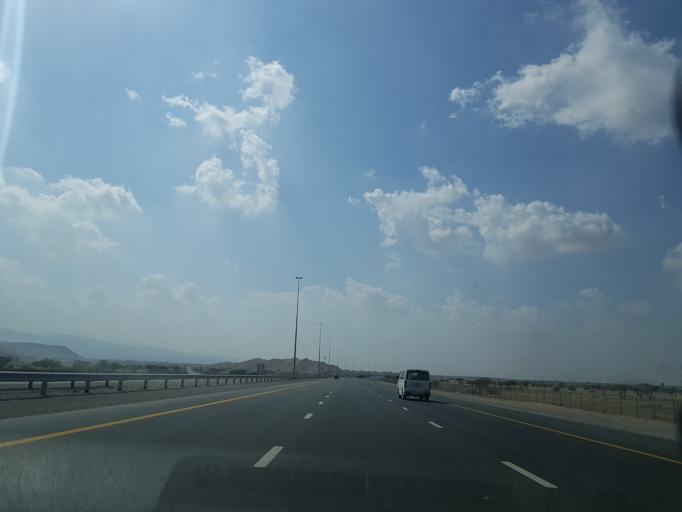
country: AE
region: Ra's al Khaymah
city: Ras al-Khaimah
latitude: 25.7400
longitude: 56.0156
